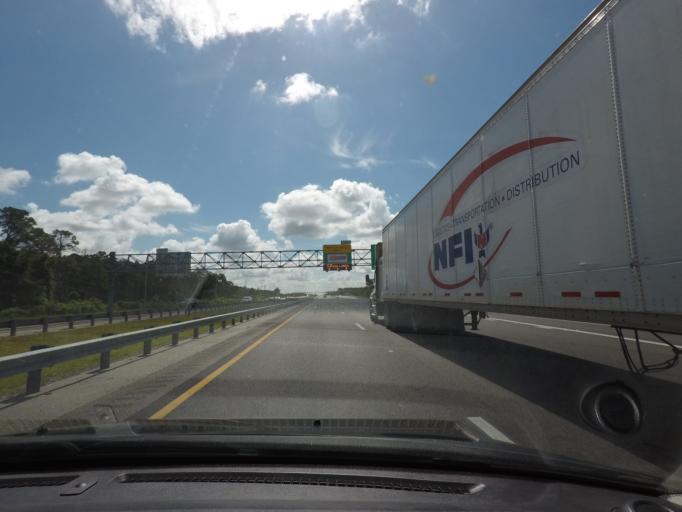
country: US
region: Florida
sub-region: Orange County
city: Alafaya
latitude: 28.4518
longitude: -81.2162
